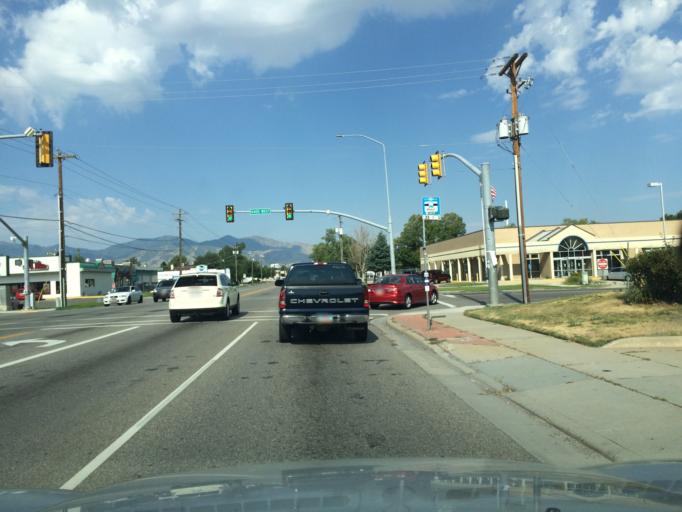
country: US
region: Utah
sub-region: Salt Lake County
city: West Valley City
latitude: 40.6967
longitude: -111.9958
